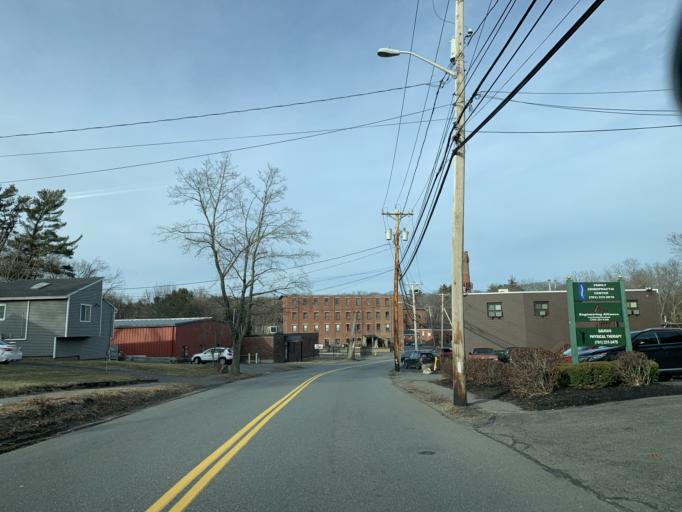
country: US
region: Massachusetts
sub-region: Essex County
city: Saugus
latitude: 42.4711
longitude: -71.0080
